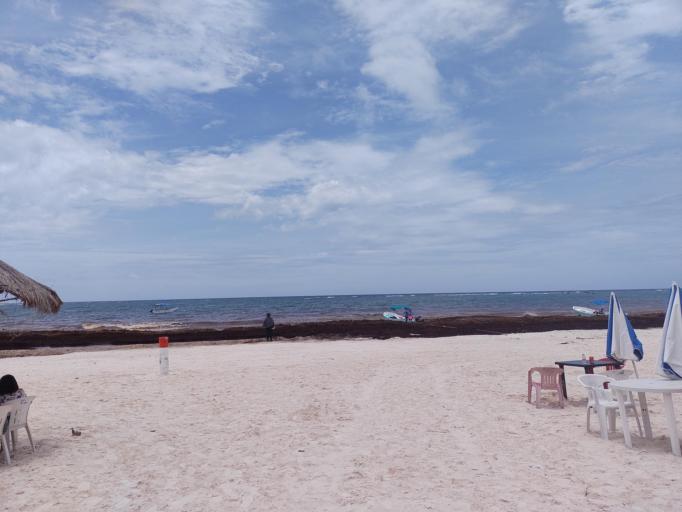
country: MX
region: Quintana Roo
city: Tulum
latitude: 20.2082
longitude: -87.4306
